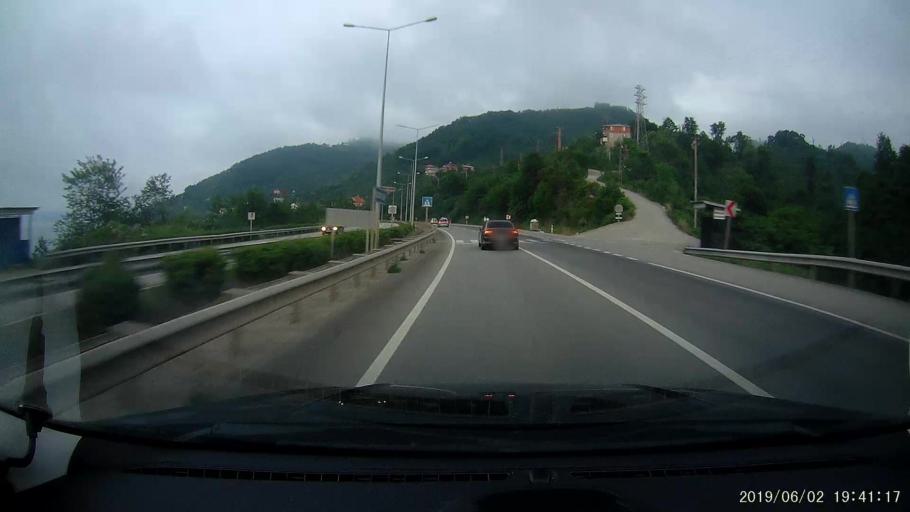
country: TR
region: Giresun
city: Kesap
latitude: 40.9146
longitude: 38.4770
